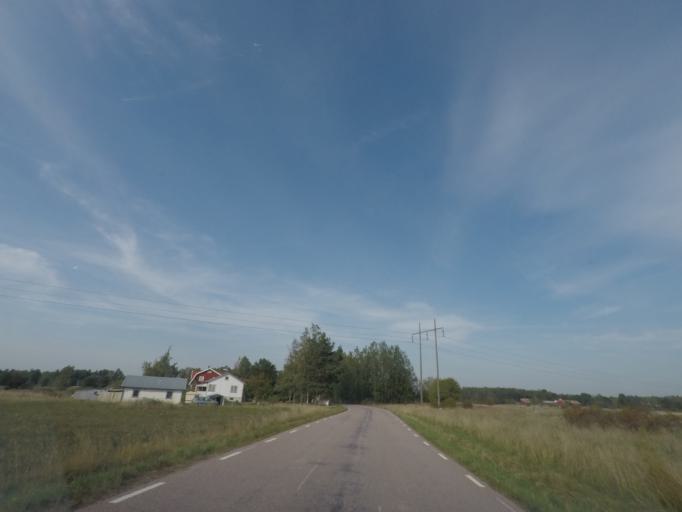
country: SE
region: Vaestmanland
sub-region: Hallstahammars Kommun
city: Kolback
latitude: 59.5310
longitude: 16.1533
